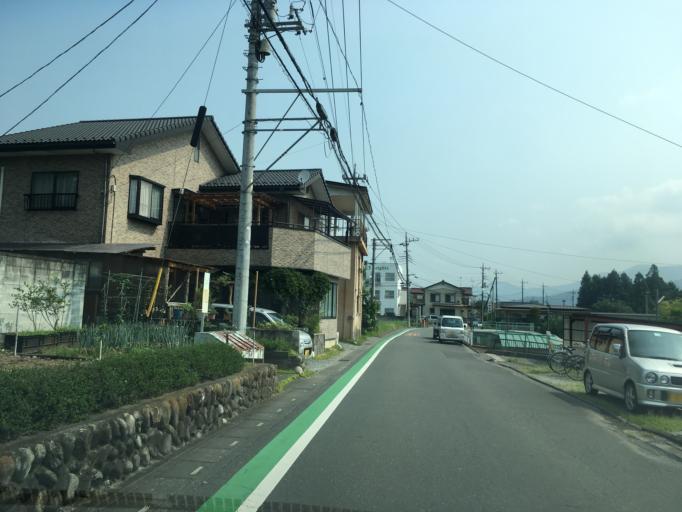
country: JP
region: Saitama
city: Chichibu
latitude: 35.9992
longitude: 139.1001
